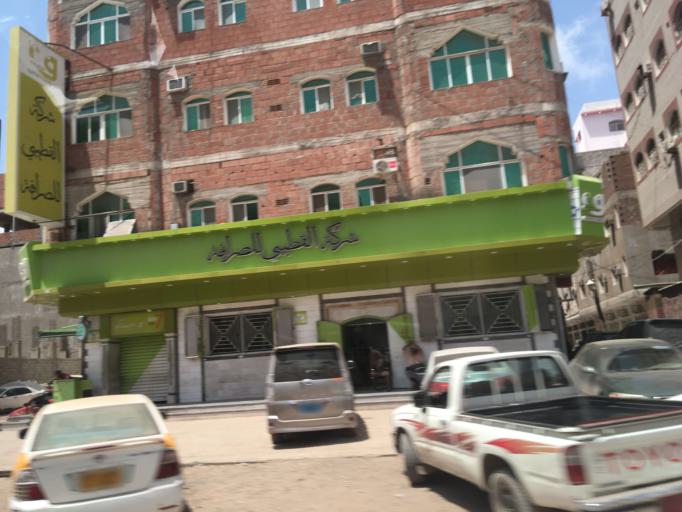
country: YE
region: Aden
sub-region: Al Mansura
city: Al Mansurah
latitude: 12.8635
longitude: 44.9714
